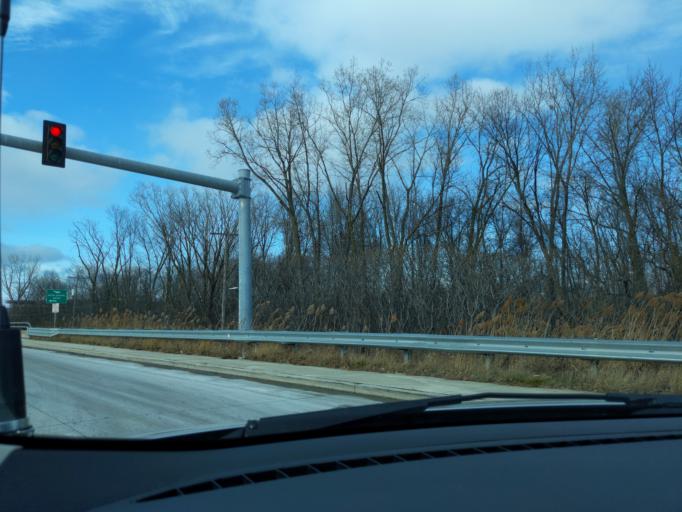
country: US
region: Wisconsin
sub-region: Brown County
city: Ashwaubenon
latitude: 44.4809
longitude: -88.0616
